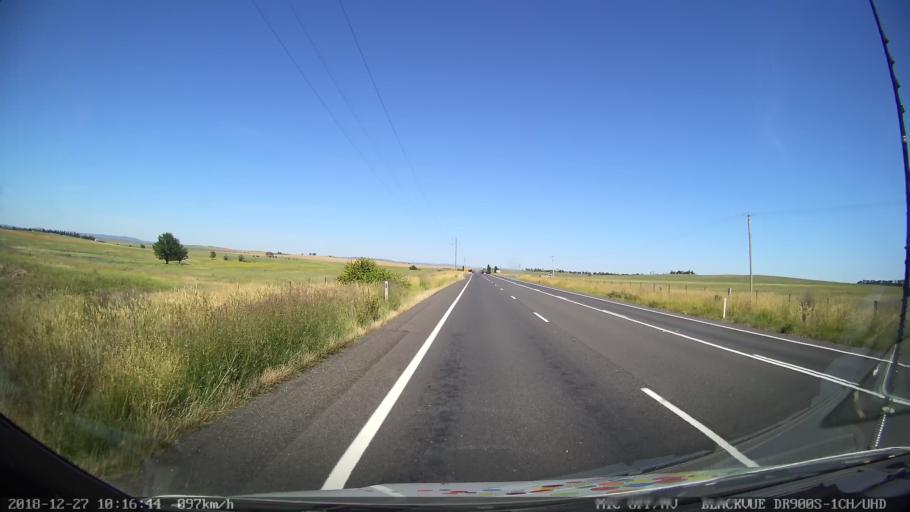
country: AU
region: New South Wales
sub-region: Bathurst Regional
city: Kelso
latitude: -33.4260
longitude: 149.6905
